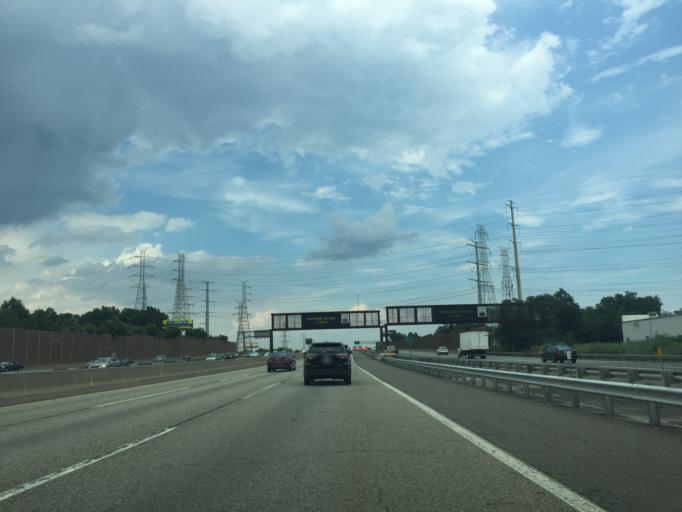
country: US
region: New Jersey
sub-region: Middlesex County
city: Port Reading
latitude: 40.5639
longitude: -74.2585
